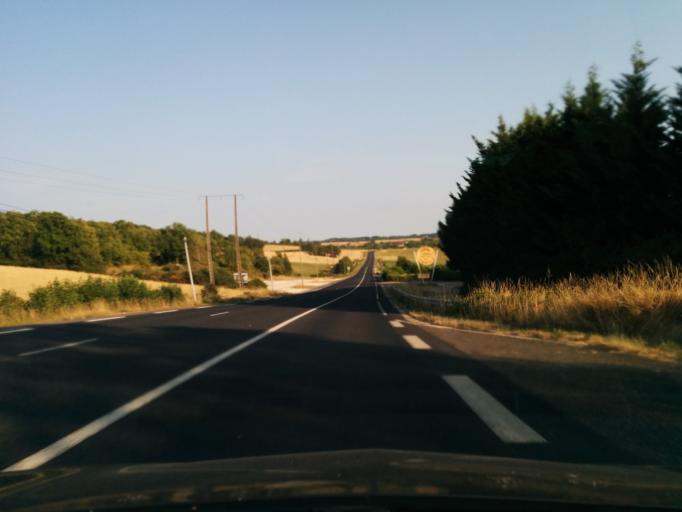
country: FR
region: Midi-Pyrenees
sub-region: Departement du Lot
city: Le Vigan
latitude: 44.7553
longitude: 1.4950
